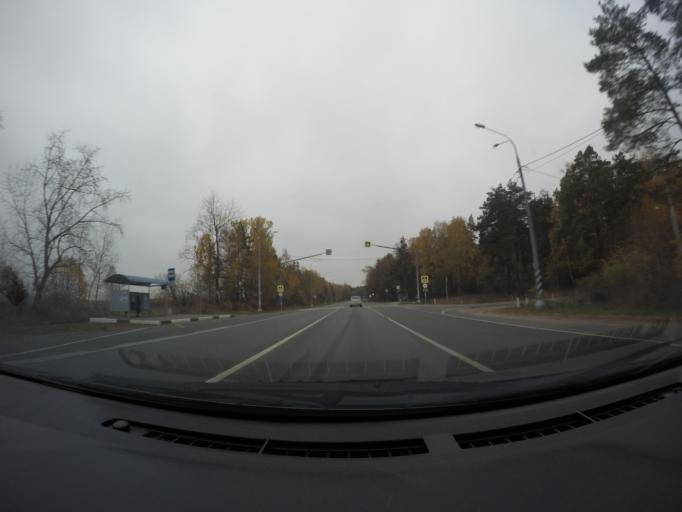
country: RU
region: Moskovskaya
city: Malyshevo
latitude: 55.4479
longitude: 38.3226
